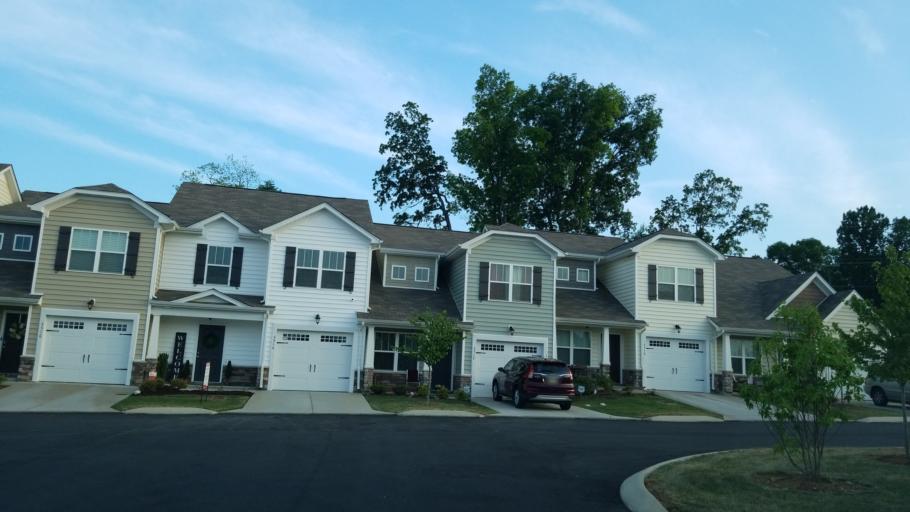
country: US
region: Tennessee
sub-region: Rutherford County
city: La Vergne
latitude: 36.0571
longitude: -86.5978
